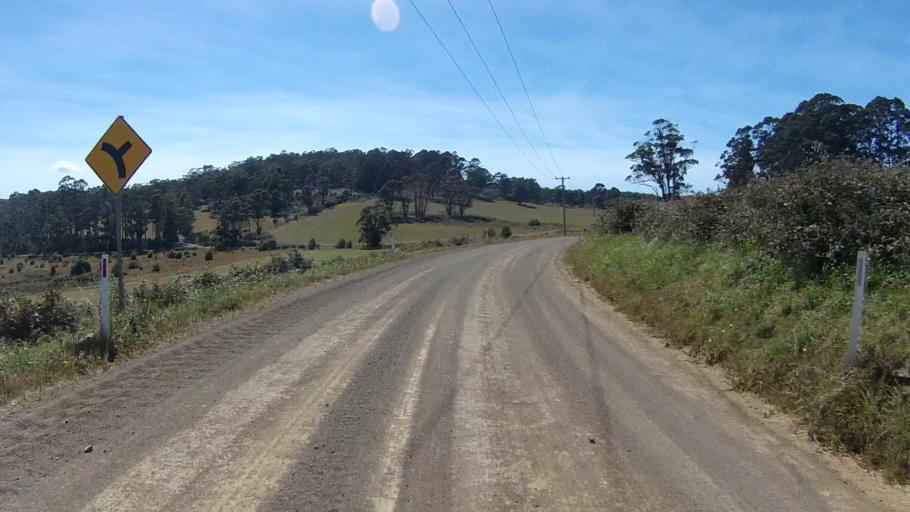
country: AU
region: Tasmania
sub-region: Sorell
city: Sorell
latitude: -42.7207
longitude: 147.7473
